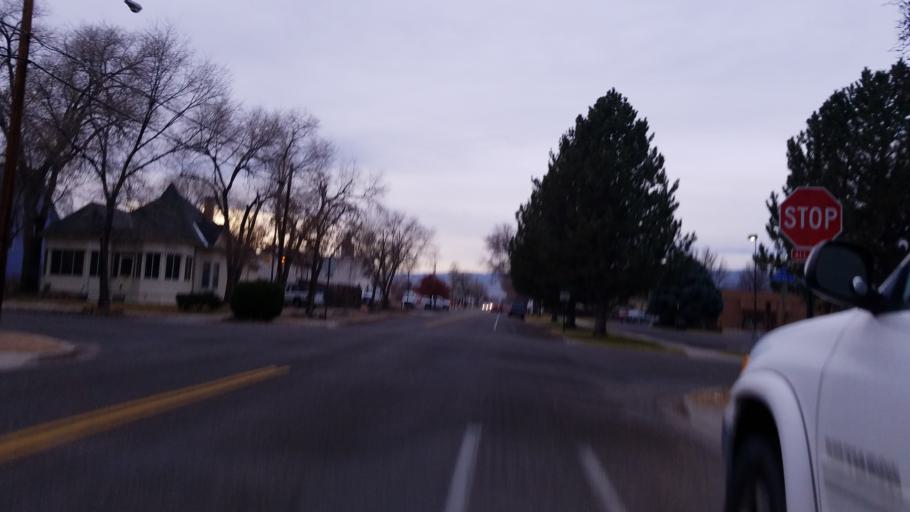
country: US
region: Colorado
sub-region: Mesa County
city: Grand Junction
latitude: 39.0717
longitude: -108.5679
